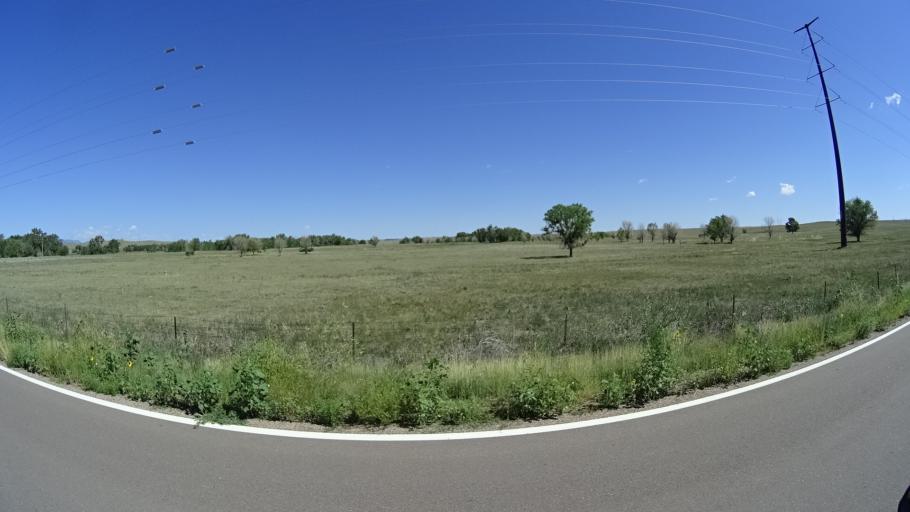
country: US
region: Colorado
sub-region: El Paso County
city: Security-Widefield
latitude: 38.7809
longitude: -104.6480
